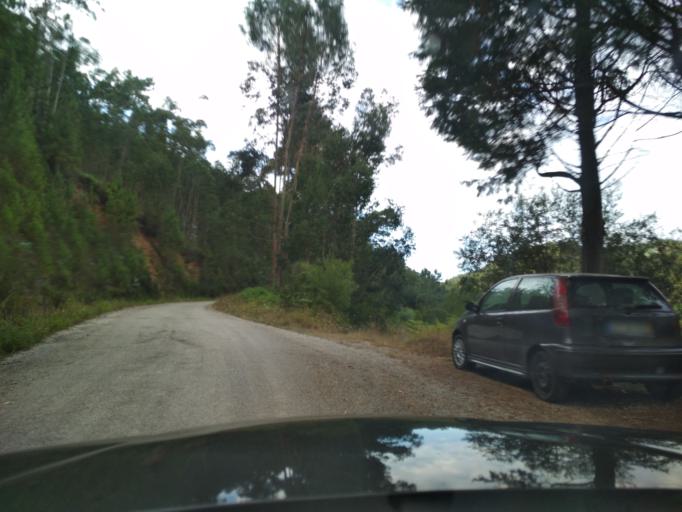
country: PT
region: Coimbra
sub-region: Coimbra
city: Coimbra
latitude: 40.2518
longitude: -8.3799
